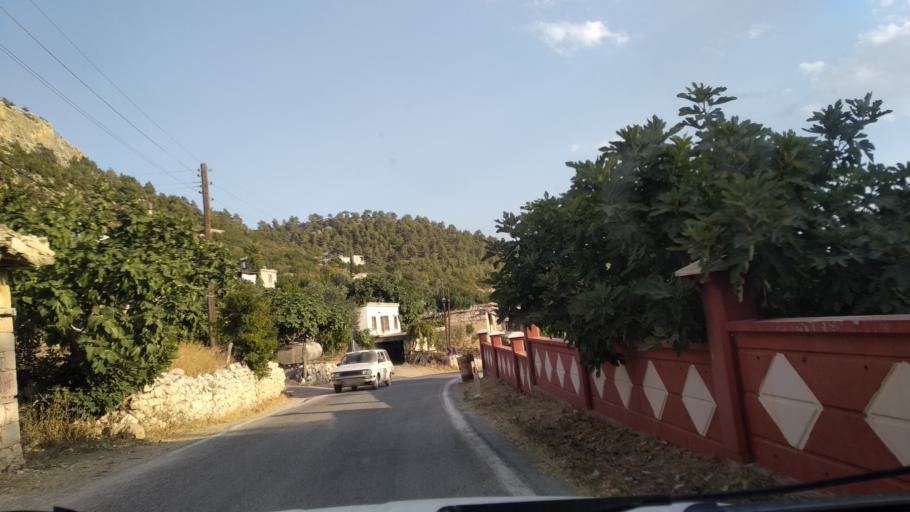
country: TR
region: Mersin
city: Sarikavak
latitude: 36.5804
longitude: 33.6441
